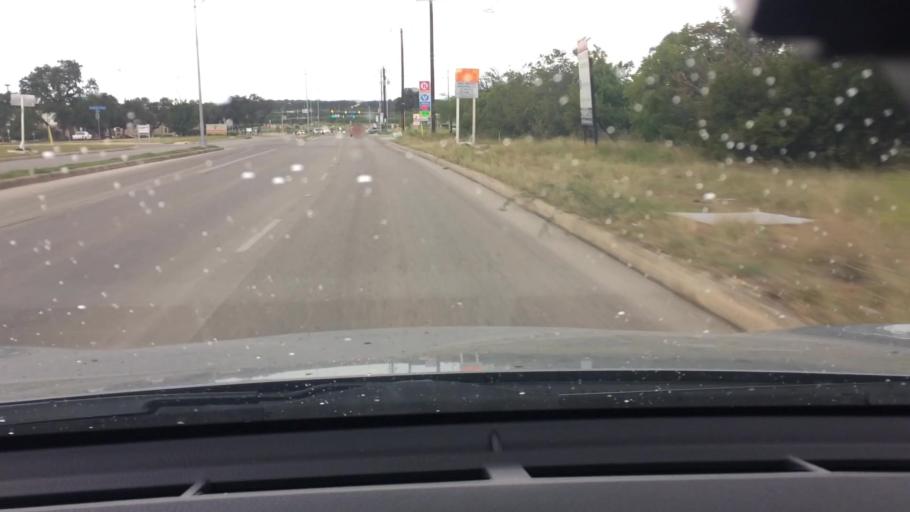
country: US
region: Texas
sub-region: Bexar County
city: Shavano Park
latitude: 29.5895
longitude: -98.5890
